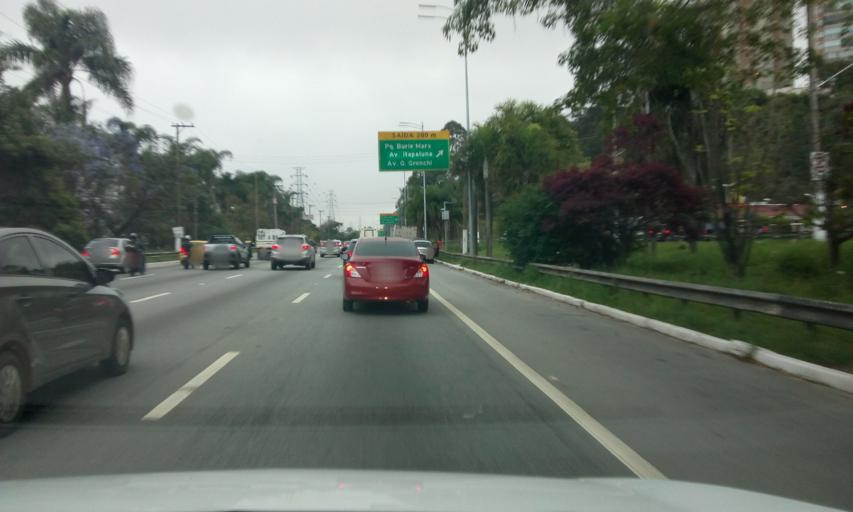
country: BR
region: Sao Paulo
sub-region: Taboao Da Serra
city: Taboao da Serra
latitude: -23.6298
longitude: -46.7165
